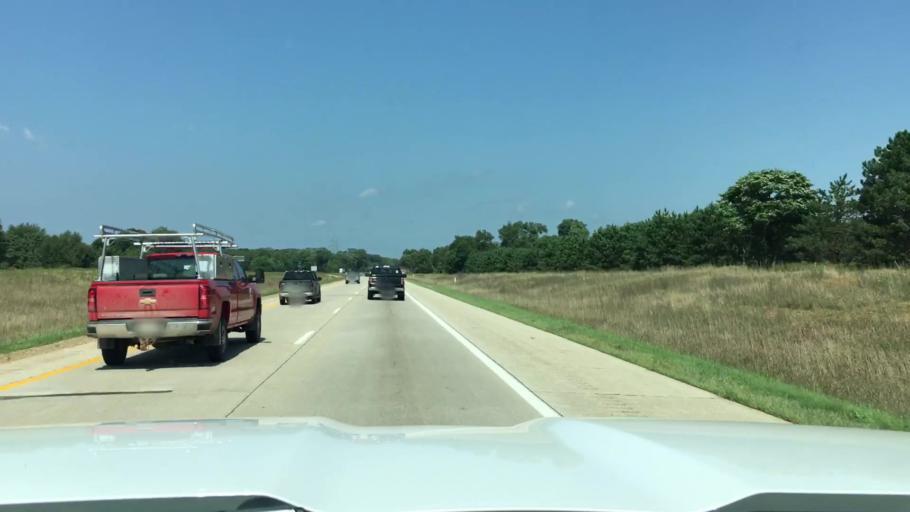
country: US
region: Michigan
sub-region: Allegan County
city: Plainwell
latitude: 42.3948
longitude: -85.6585
